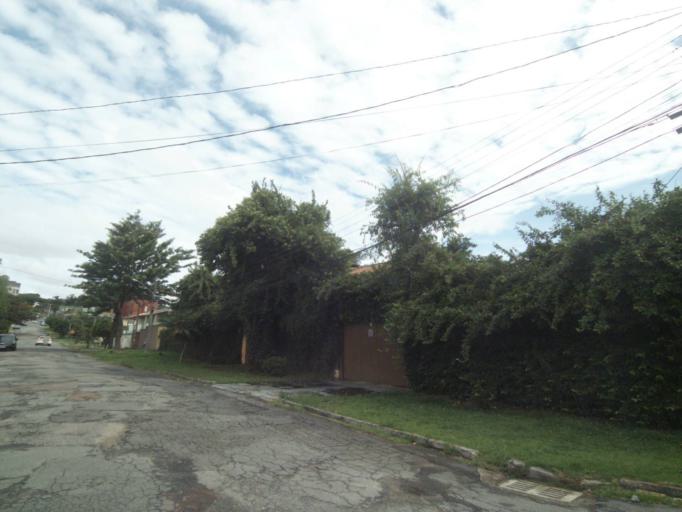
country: BR
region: Parana
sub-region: Curitiba
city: Curitiba
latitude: -25.4338
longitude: -49.3137
